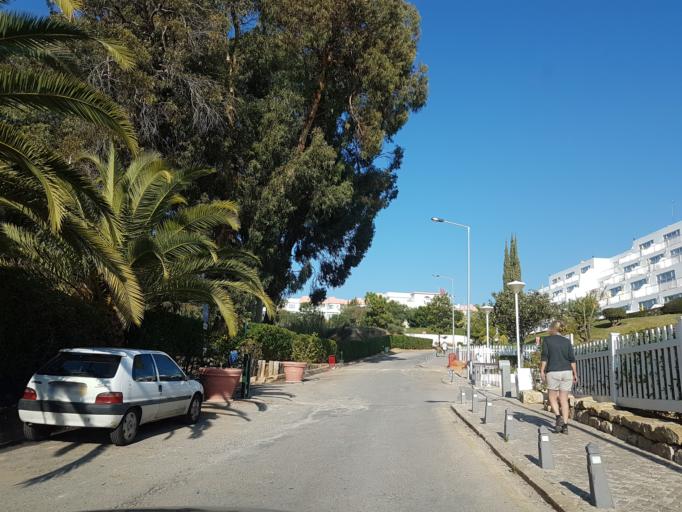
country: PT
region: Faro
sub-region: Albufeira
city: Albufeira
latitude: 37.0884
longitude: -8.2241
